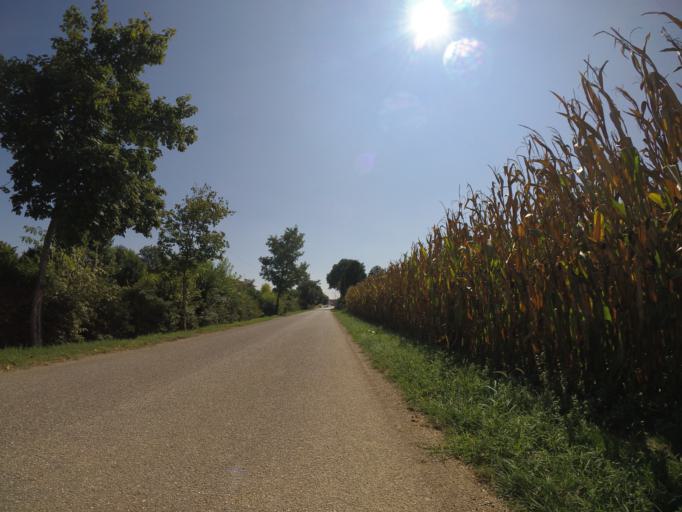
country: IT
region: Friuli Venezia Giulia
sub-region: Provincia di Udine
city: Talmassons
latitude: 45.9385
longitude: 13.0903
